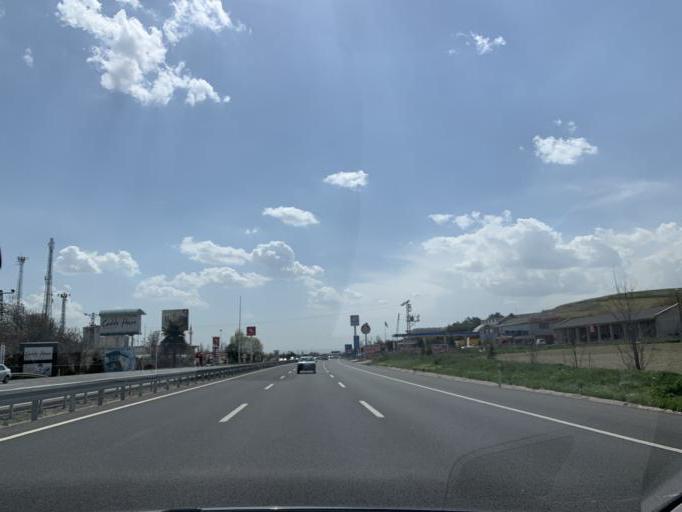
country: TR
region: Ankara
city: Etimesgut
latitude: 39.8225
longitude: 32.5715
